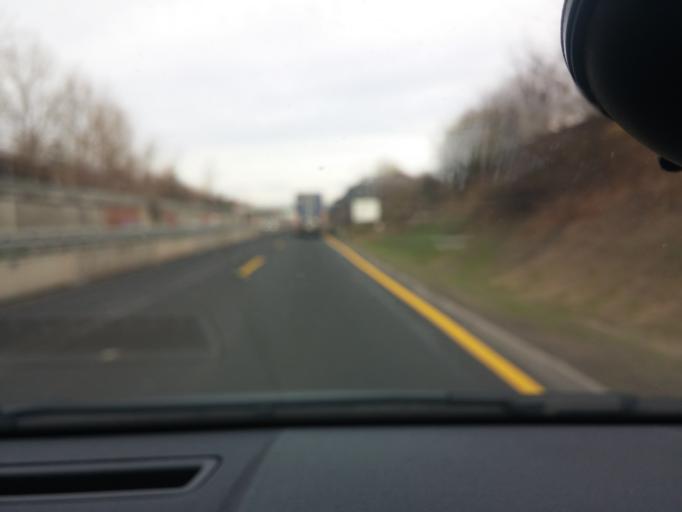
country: DE
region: Hesse
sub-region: Regierungsbezirk Darmstadt
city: Rodgau
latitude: 50.0482
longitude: 8.8906
